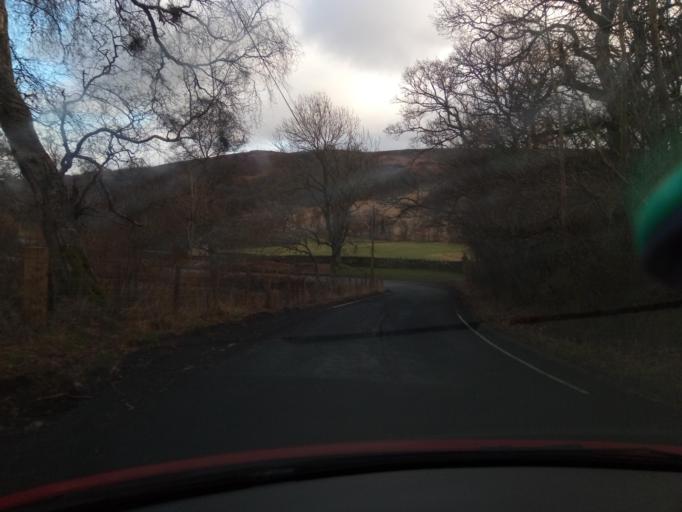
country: GB
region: England
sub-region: Northumberland
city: Otterburn
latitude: 55.2688
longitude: -2.0870
